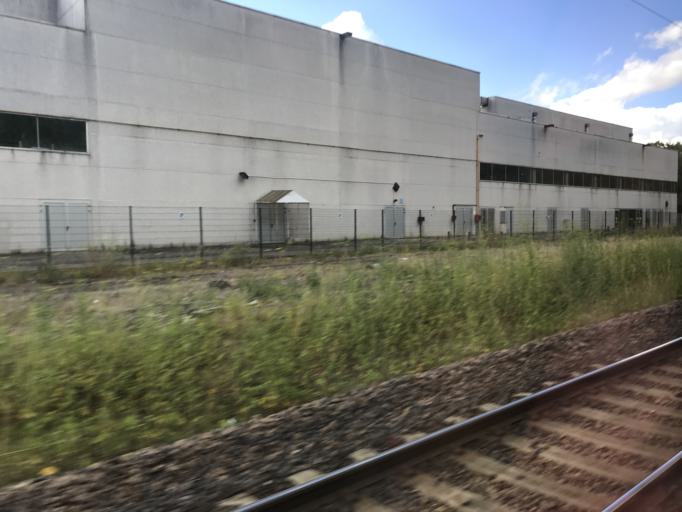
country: FR
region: Lorraine
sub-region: Departement de Meurthe-et-Moselle
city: Herserange
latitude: 49.5240
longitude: 5.7768
